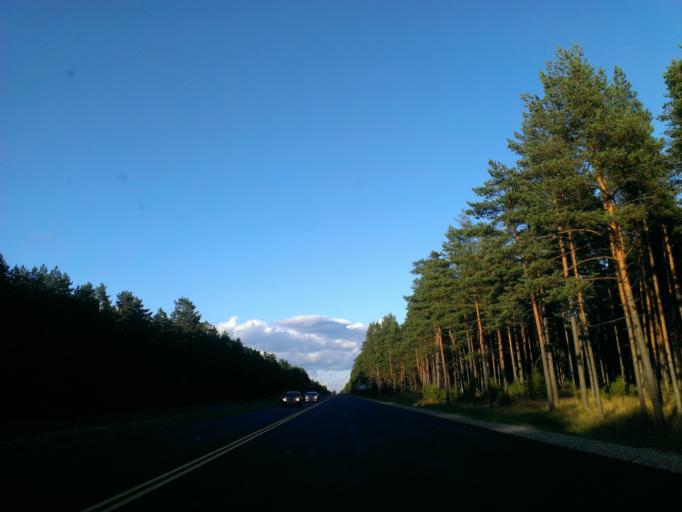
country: LV
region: Riga
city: Bergi
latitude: 57.0217
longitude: 24.3445
